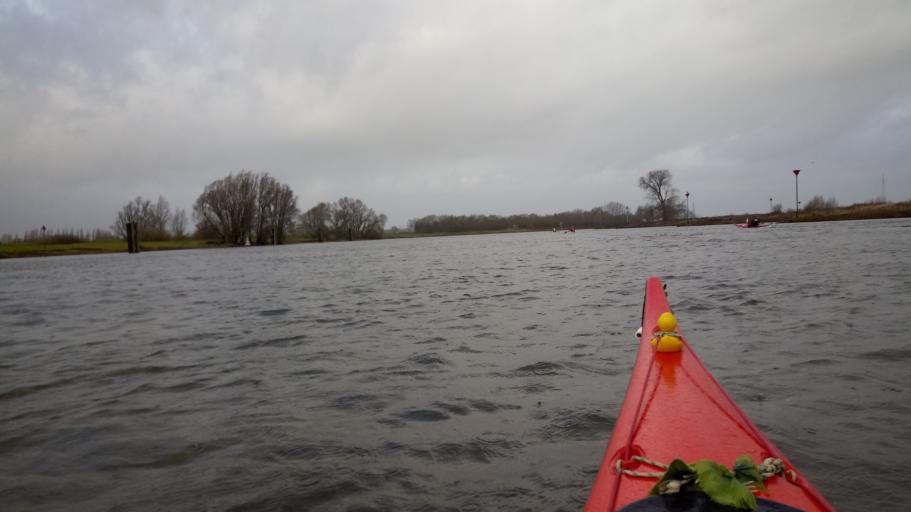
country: NL
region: Gelderland
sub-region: Gemeente Zutphen
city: Zutphen
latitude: 52.1478
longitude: 6.1857
